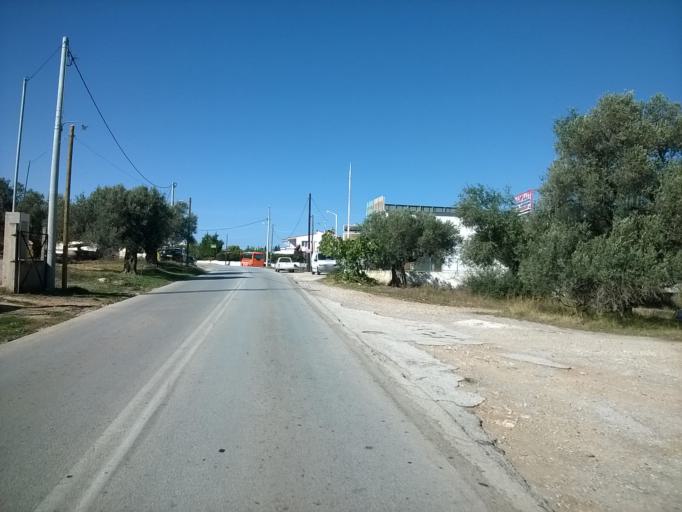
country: GR
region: Attica
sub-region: Nomarchia Anatolikis Attikis
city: Keratea
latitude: 37.8033
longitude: 23.9912
